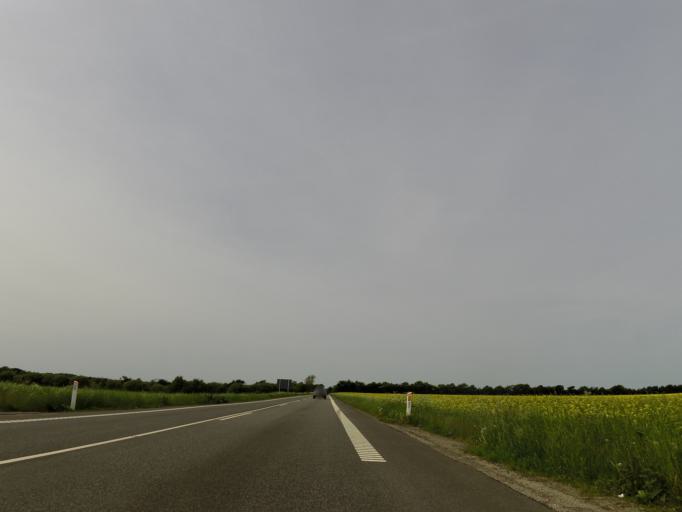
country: DK
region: Central Jutland
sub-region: Holstebro Kommune
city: Vinderup
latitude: 56.5702
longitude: 8.8689
